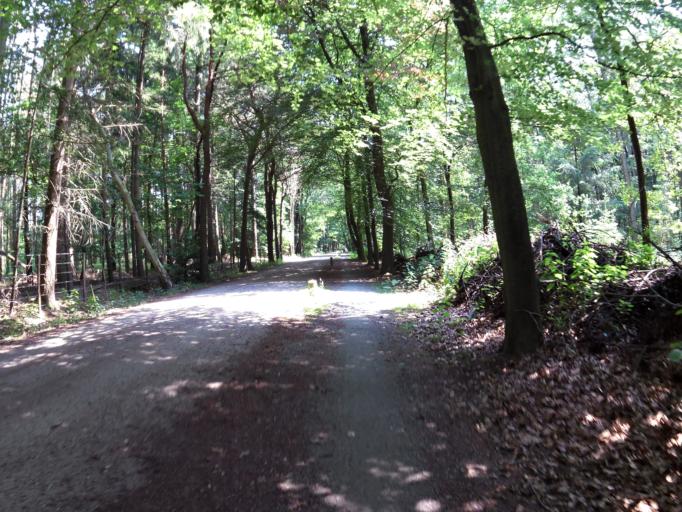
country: NL
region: North Brabant
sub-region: Gemeente Boxtel
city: Boxtel
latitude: 51.6189
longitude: 5.3297
